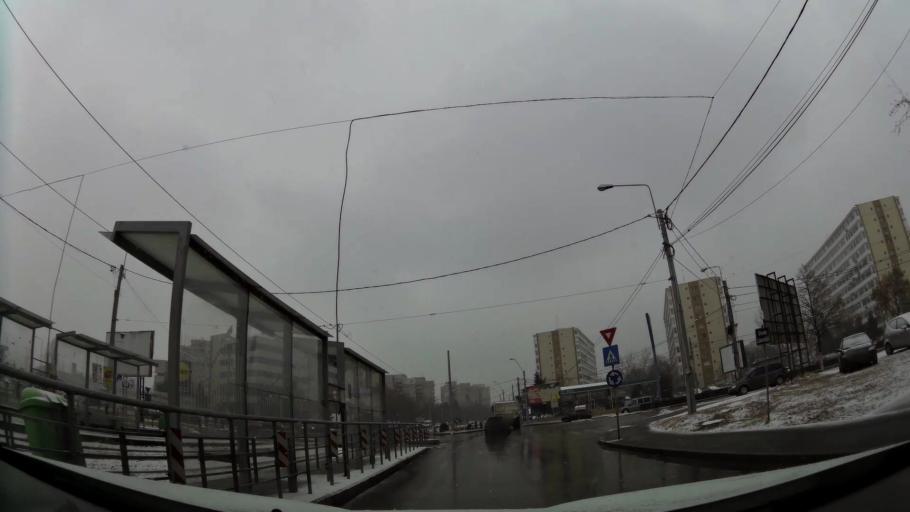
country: RO
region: Prahova
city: Ploiesti
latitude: 44.9280
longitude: 25.9926
